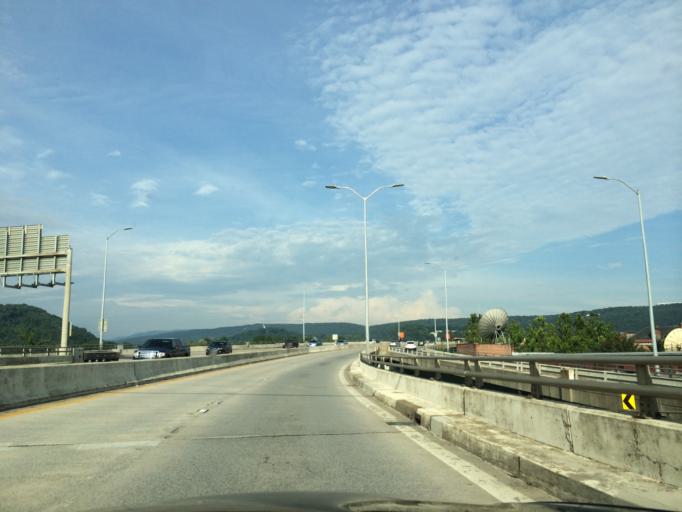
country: US
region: Maryland
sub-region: Allegany County
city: Cumberland
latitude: 39.6492
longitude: -78.7612
